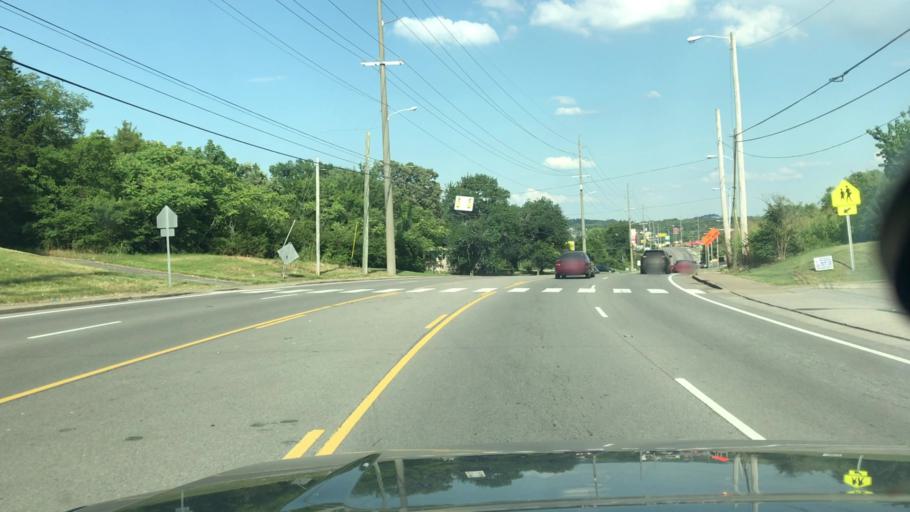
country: US
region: Tennessee
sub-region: Davidson County
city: Nashville
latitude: 36.2084
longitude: -86.7883
